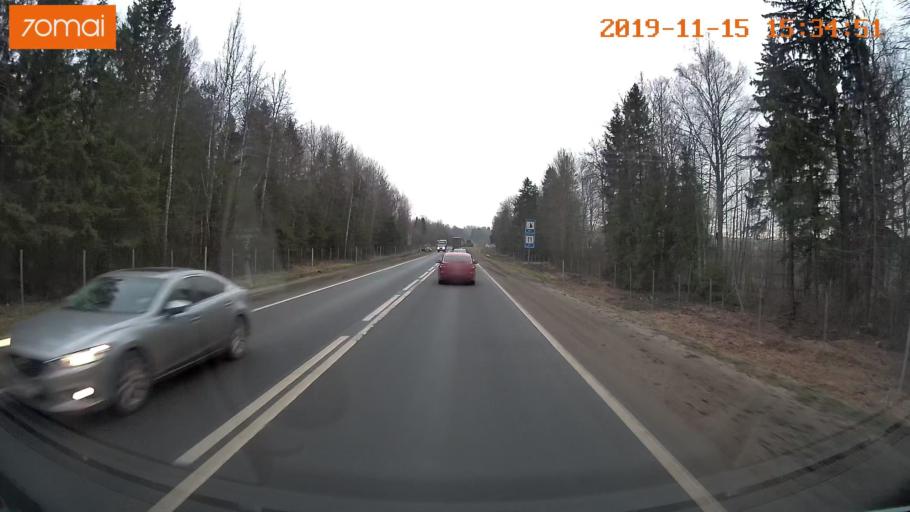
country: RU
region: Jaroslavl
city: Danilov
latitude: 58.0651
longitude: 40.0881
